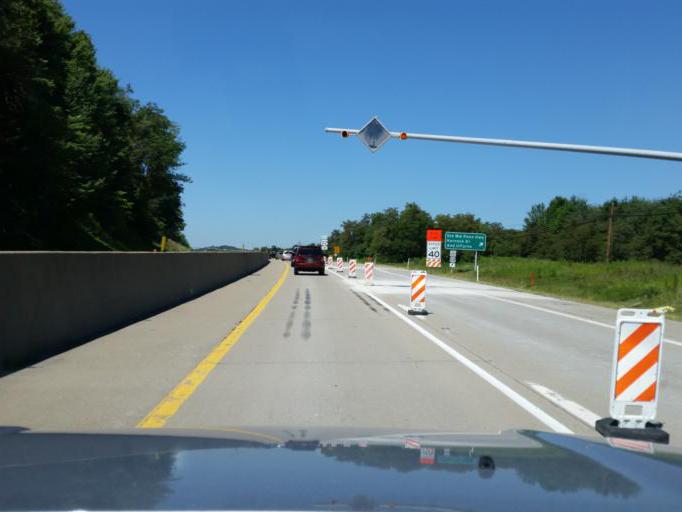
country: US
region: Pennsylvania
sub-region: Westmoreland County
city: Delmont
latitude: 40.3980
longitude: -79.4621
